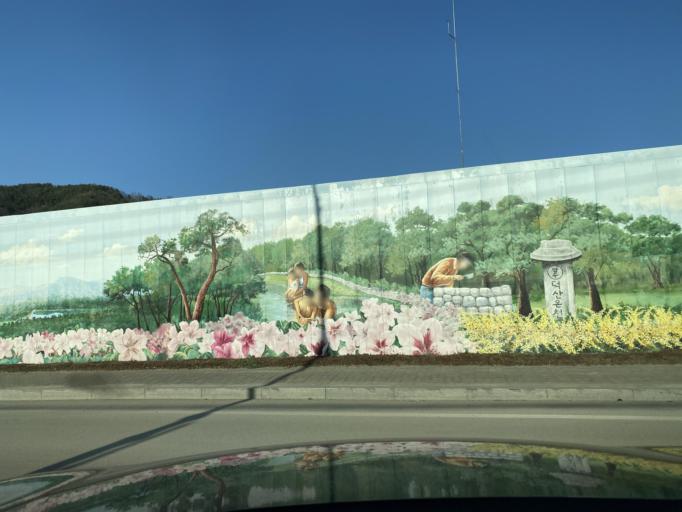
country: KR
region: Chungcheongnam-do
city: Yesan
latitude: 36.6793
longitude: 126.8613
